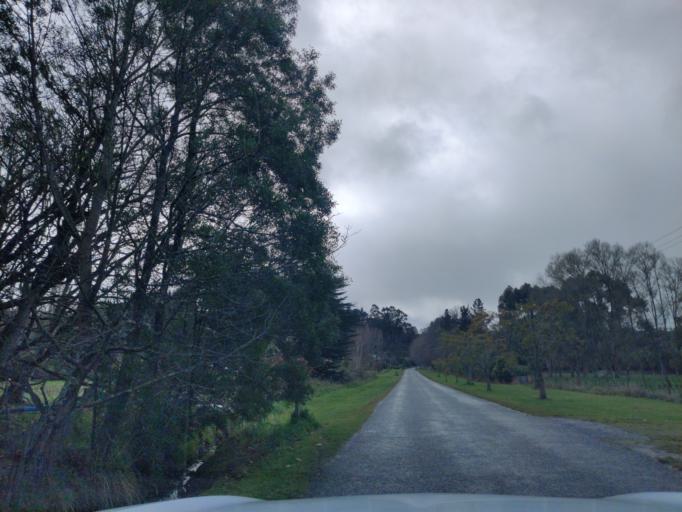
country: NZ
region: Manawatu-Wanganui
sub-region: Palmerston North City
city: Palmerston North
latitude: -40.1704
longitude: 175.7990
